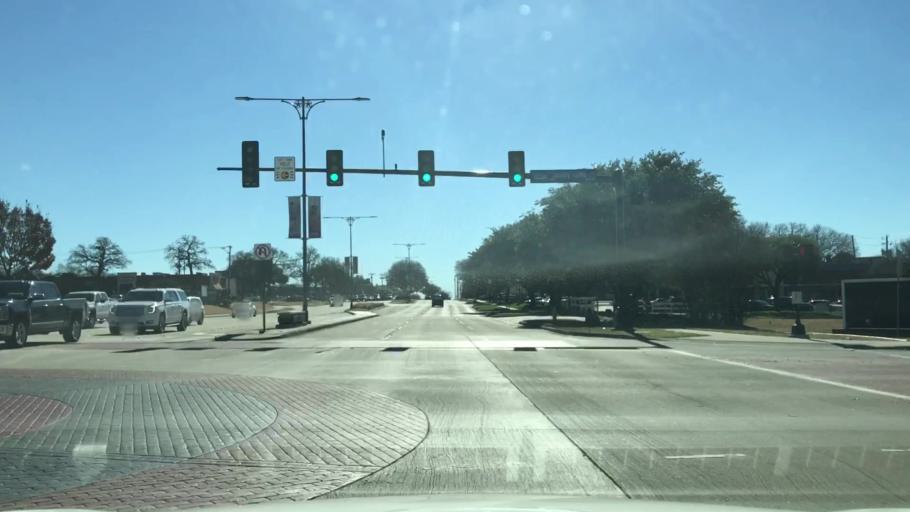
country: US
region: Texas
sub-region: Dallas County
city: Coppell
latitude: 32.9694
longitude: -96.9937
